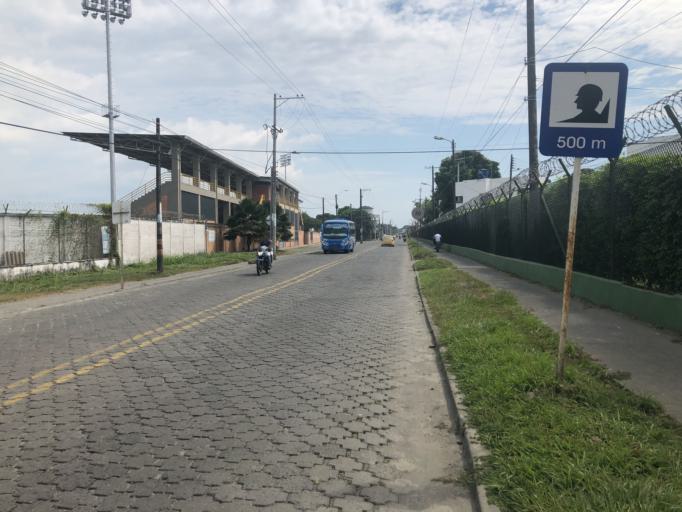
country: CO
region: Narino
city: Tumaco
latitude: 1.8213
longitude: -78.7457
